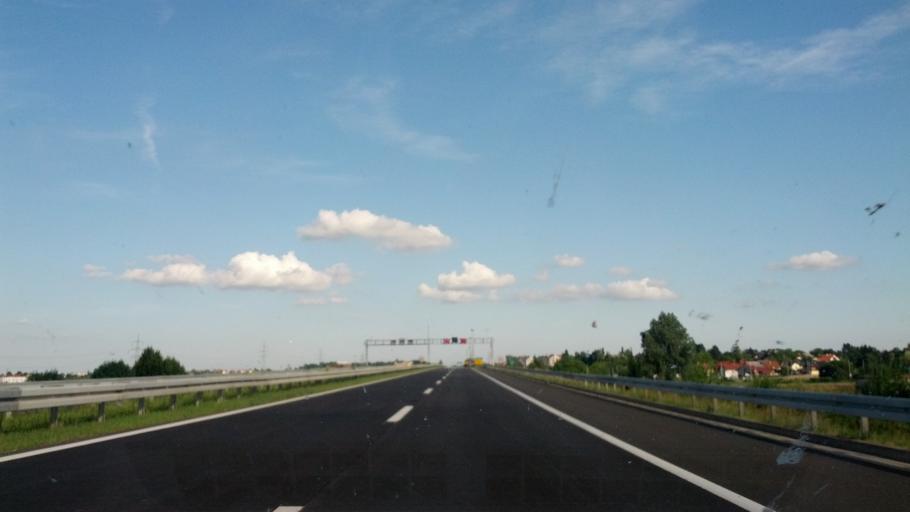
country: HR
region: Zagrebacka
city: Bestovje
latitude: 45.8039
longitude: 15.7766
